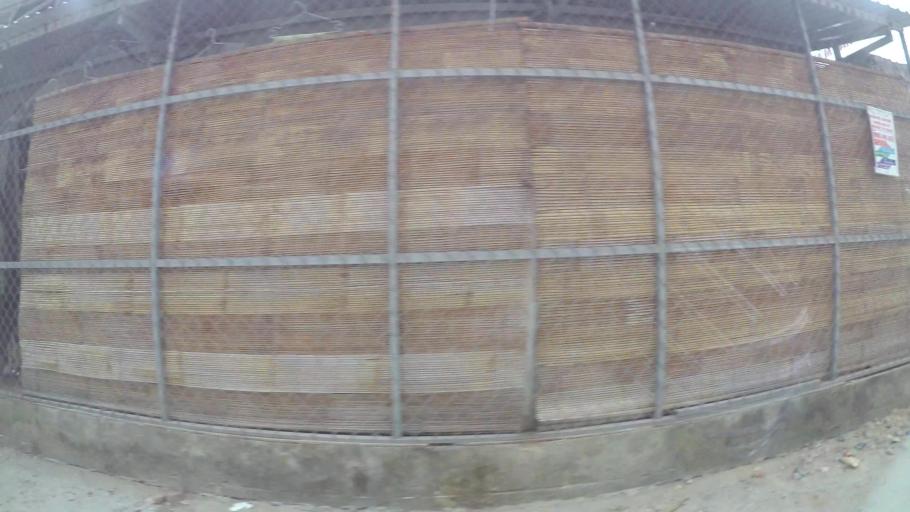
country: VN
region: Da Nang
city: Thanh Khe
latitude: 16.0718
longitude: 108.1948
